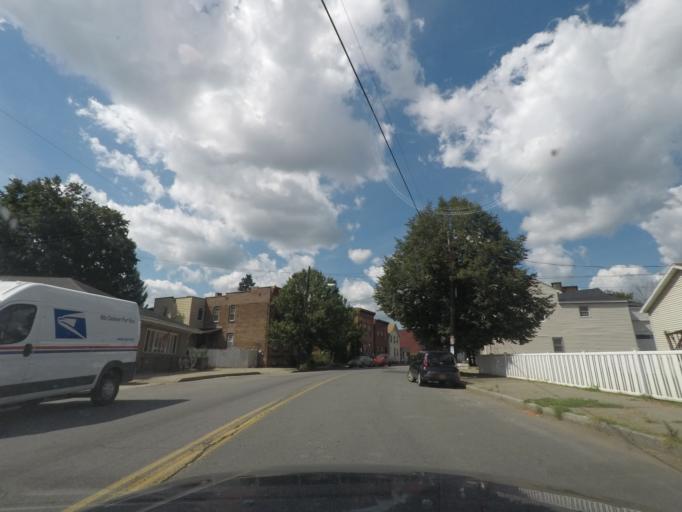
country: US
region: New York
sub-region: Rensselaer County
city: Troy
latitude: 42.7202
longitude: -73.6872
